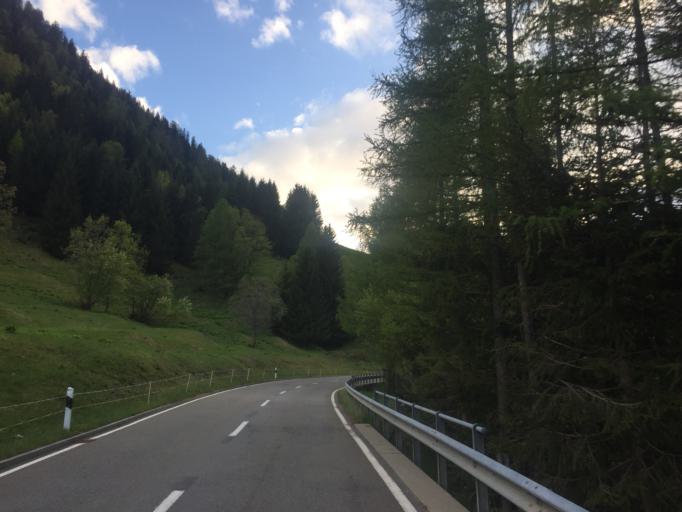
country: CH
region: Ticino
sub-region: Leventina District
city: Airolo
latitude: 46.5115
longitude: 8.5349
